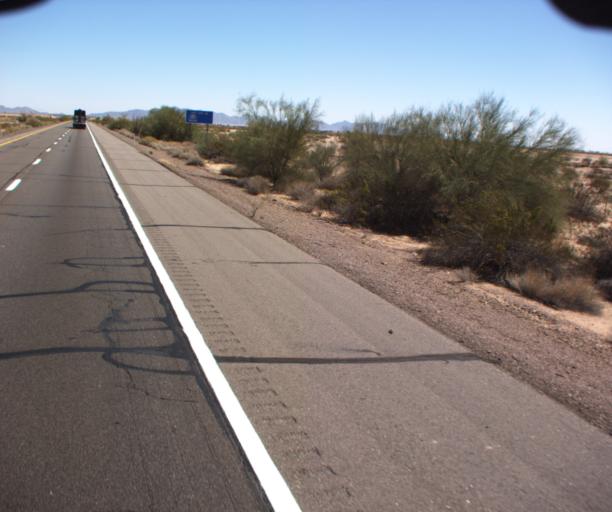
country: US
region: Arizona
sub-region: Yuma County
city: Wellton
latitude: 32.6913
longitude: -113.9667
